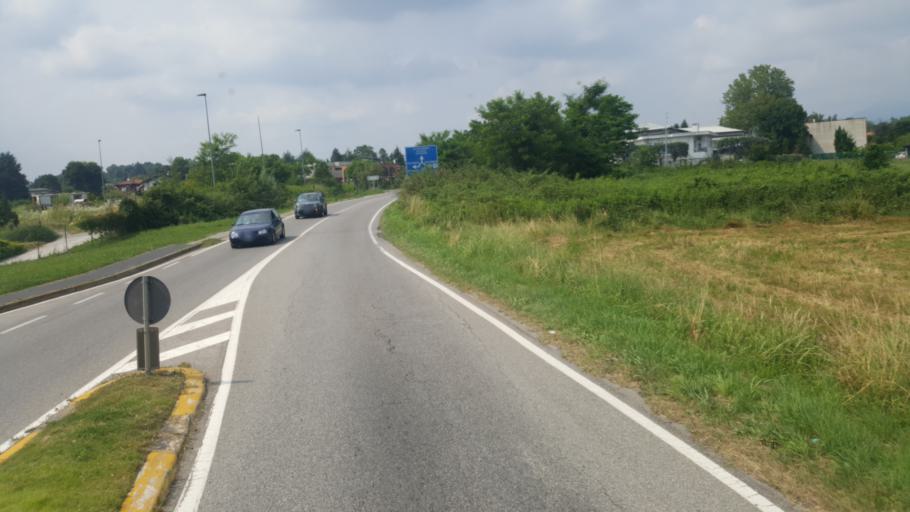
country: IT
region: Lombardy
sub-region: Provincia di Como
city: Olgiate Comasco
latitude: 45.7841
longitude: 8.9574
